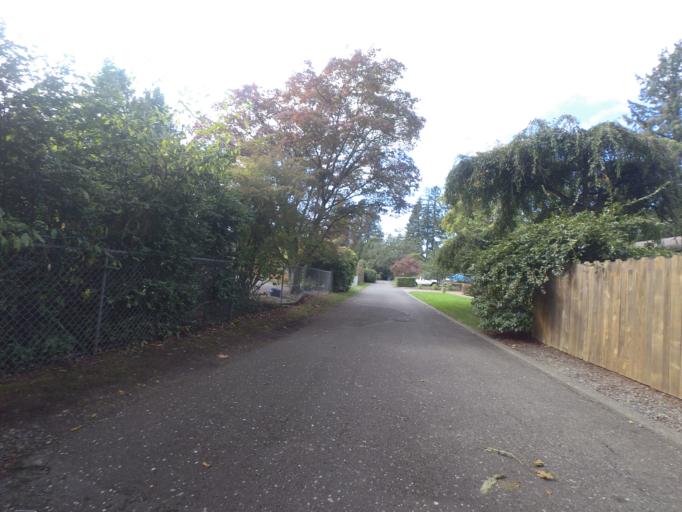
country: US
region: Washington
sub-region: Pierce County
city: Lakewood
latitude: 47.1692
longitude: -122.5444
